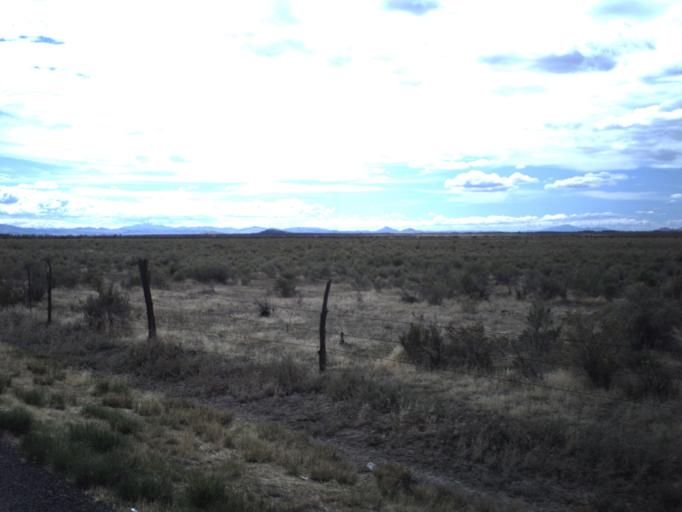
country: US
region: Utah
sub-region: Millard County
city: Fillmore
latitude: 39.0783
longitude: -112.4099
